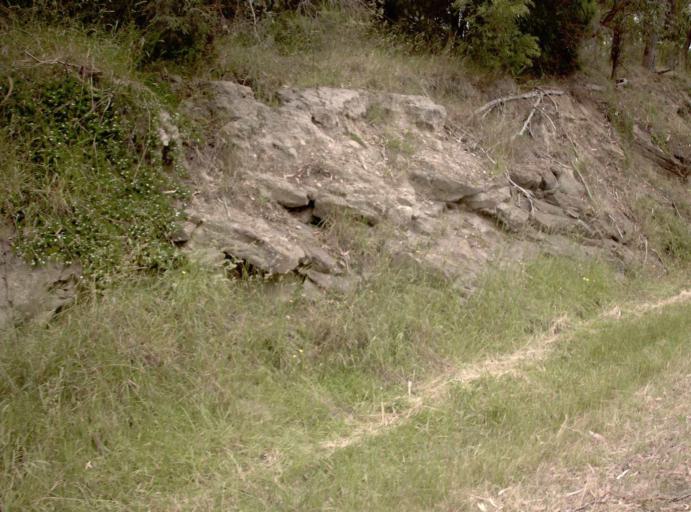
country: AU
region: Victoria
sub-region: Latrobe
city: Traralgon
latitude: -38.4875
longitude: 146.6381
